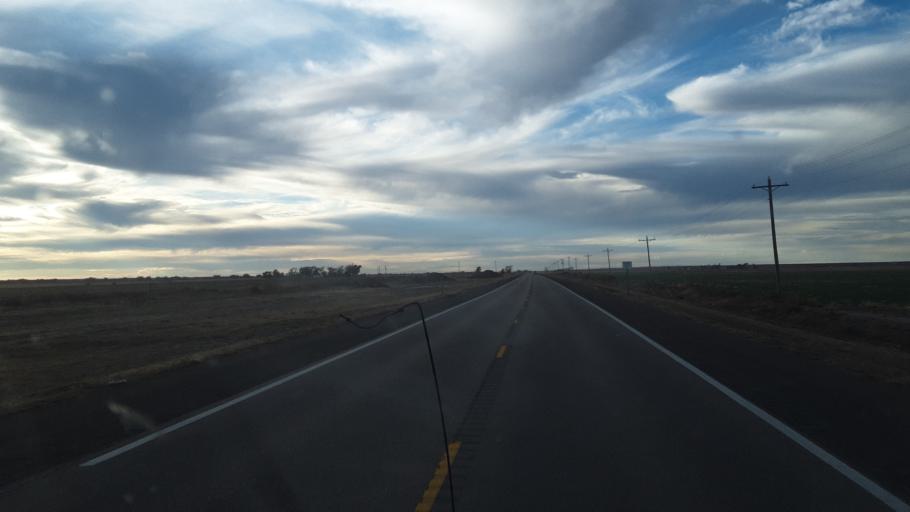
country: US
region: Kansas
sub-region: Hamilton County
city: Syracuse
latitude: 38.0151
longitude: -101.8841
